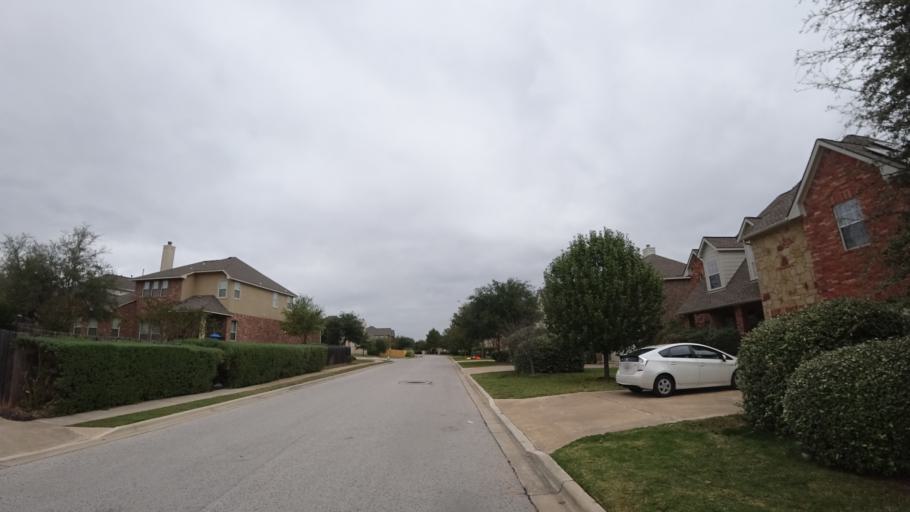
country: US
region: Texas
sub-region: Travis County
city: Bee Cave
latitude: 30.3522
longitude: -97.9040
